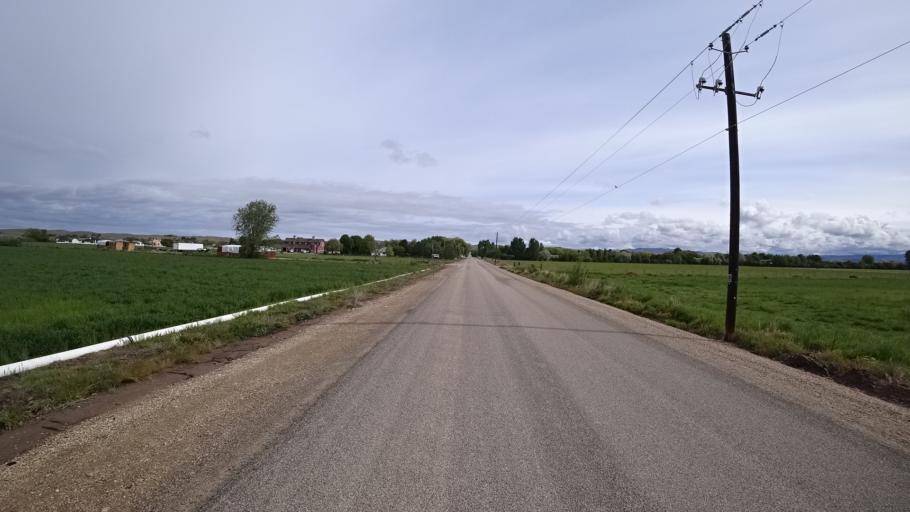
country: US
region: Idaho
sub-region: Ada County
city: Eagle
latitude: 43.7224
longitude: -116.4035
